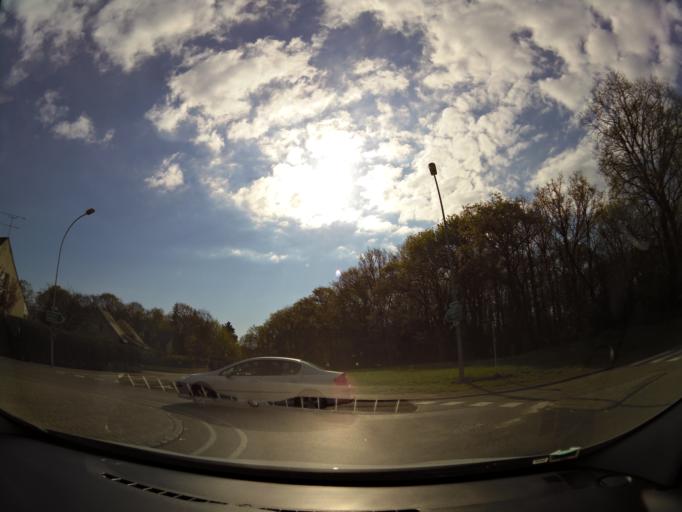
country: FR
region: Brittany
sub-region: Departement d'Ille-et-Vilaine
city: Laille
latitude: 47.9749
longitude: -1.7206
